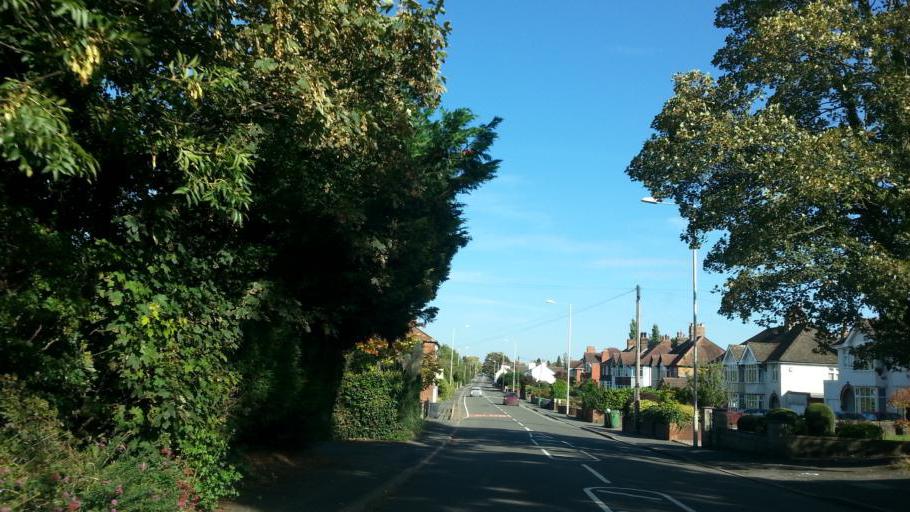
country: GB
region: England
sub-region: Telford and Wrekin
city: Wellington
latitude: 52.6930
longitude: -2.5307
